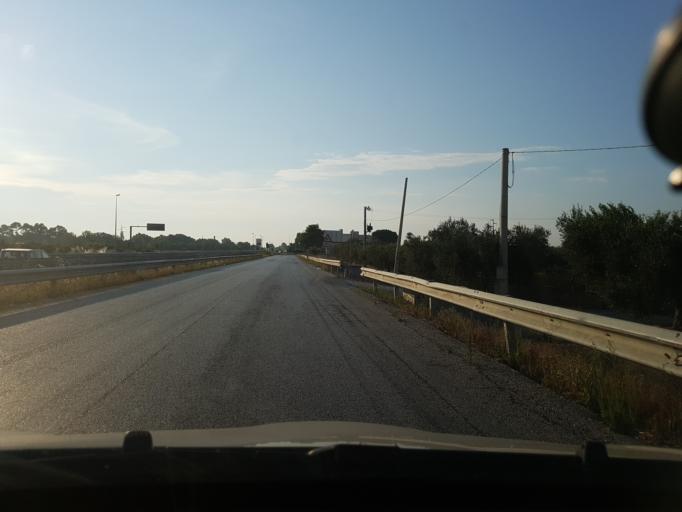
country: IT
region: Apulia
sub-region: Provincia di Foggia
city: Carapelle
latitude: 41.3958
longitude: 15.6589
